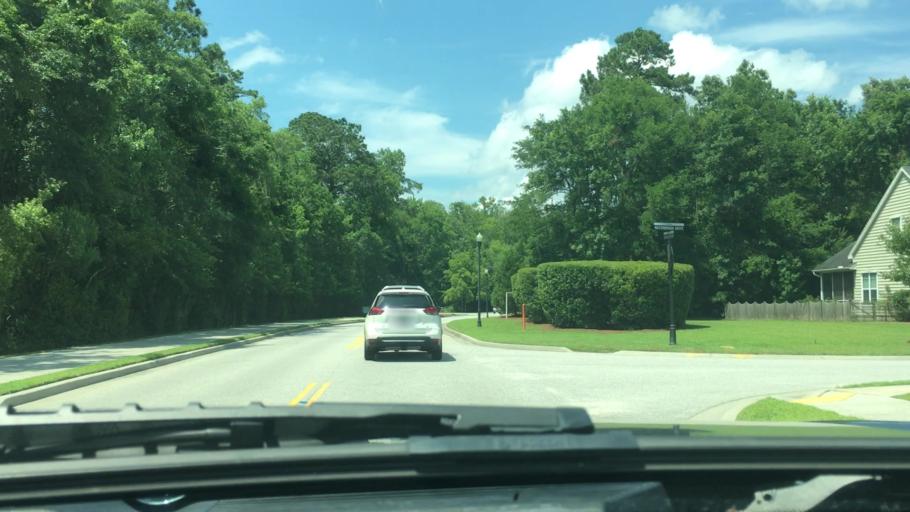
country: US
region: South Carolina
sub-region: Charleston County
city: Shell Point
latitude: 32.8041
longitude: -80.0802
